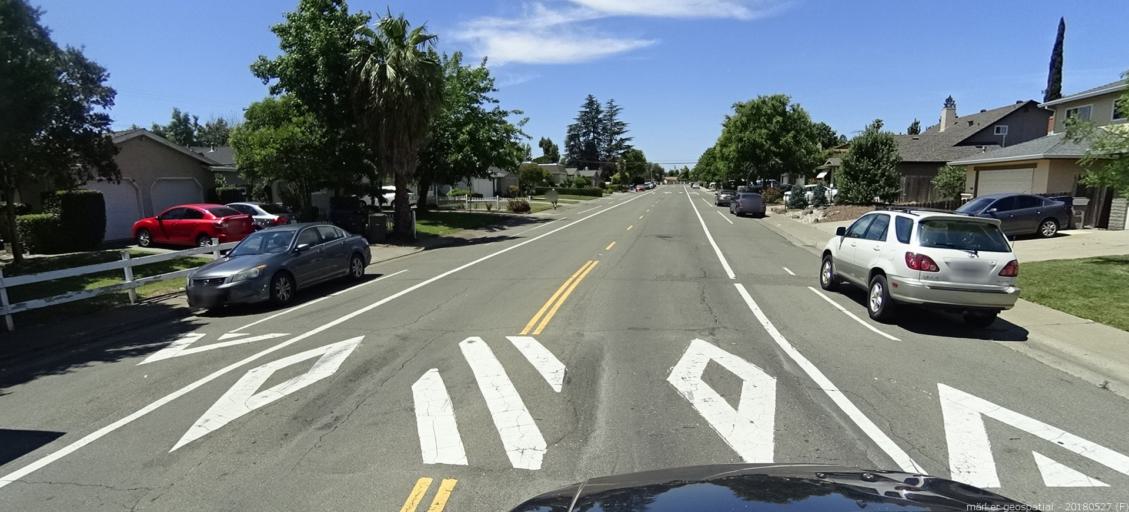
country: US
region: California
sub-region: Sacramento County
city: Rosemont
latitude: 38.5499
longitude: -121.3958
